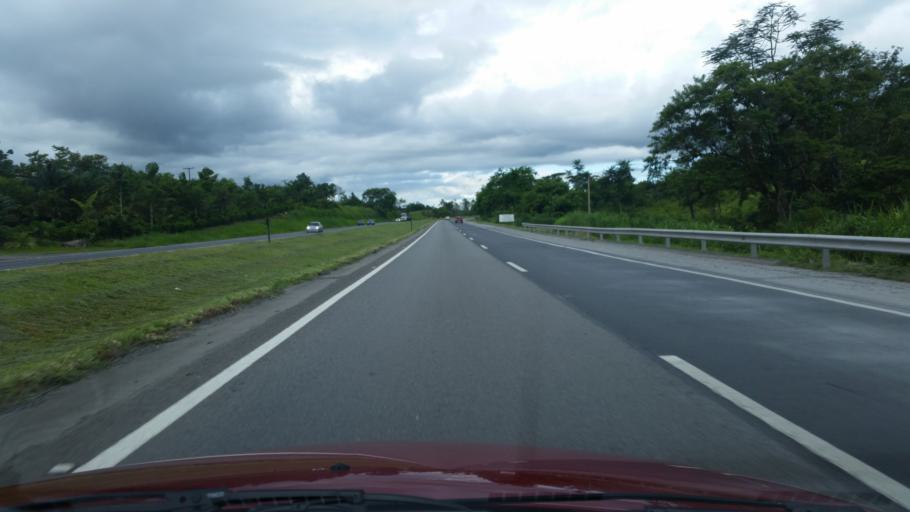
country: BR
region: Sao Paulo
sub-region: Miracatu
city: Miracatu
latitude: -24.2821
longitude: -47.4326
